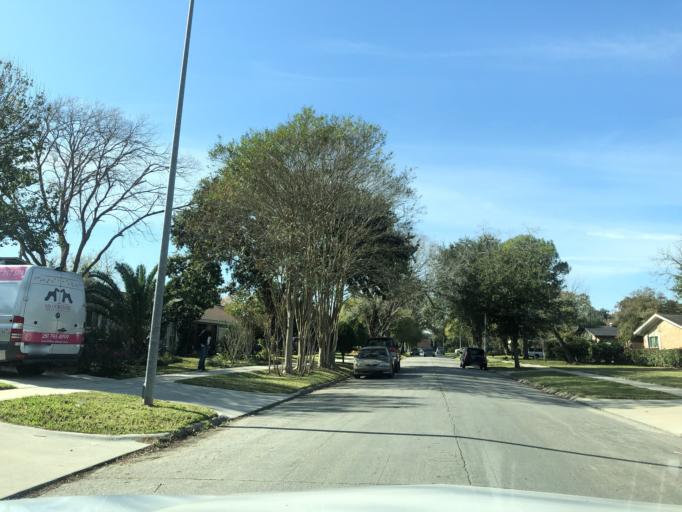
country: US
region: Texas
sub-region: Harris County
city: Bellaire
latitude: 29.6816
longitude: -95.5060
